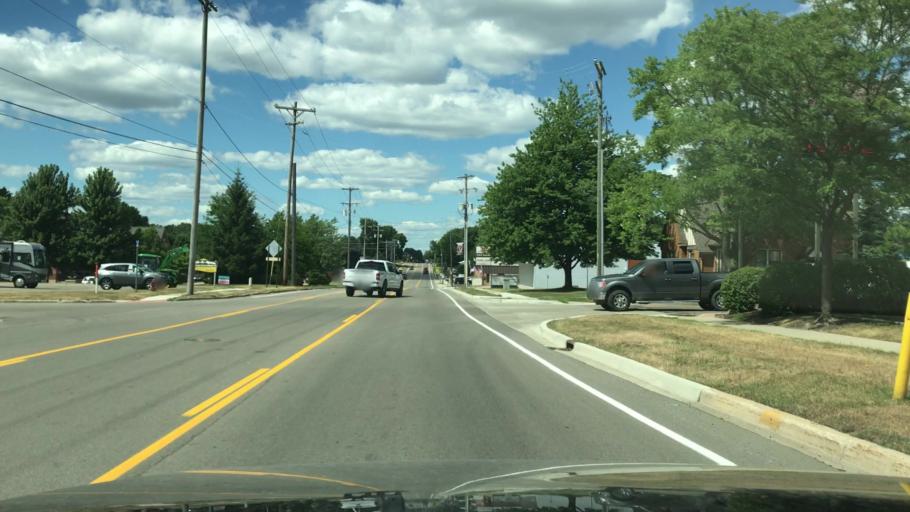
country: US
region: Michigan
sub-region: Kent County
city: Byron Center
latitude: 42.8130
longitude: -85.7229
